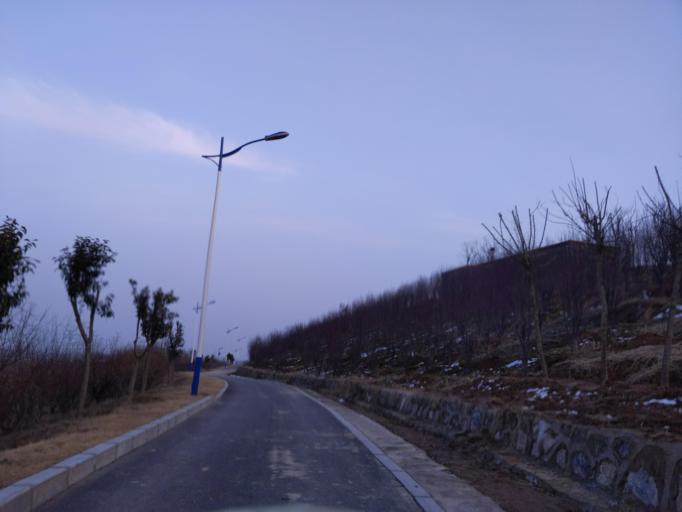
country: CN
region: Henan Sheng
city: Zhongyuanlu
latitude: 35.8167
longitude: 115.0558
